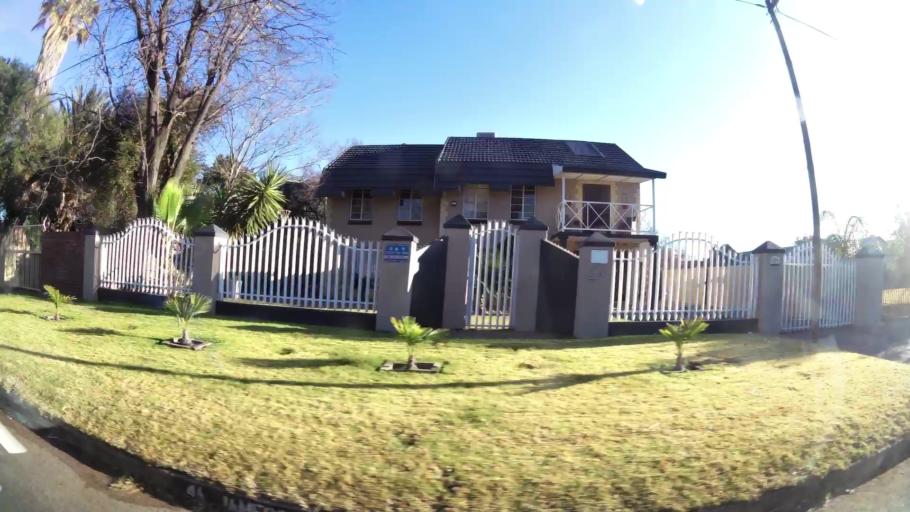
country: ZA
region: Northern Cape
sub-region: Frances Baard District Municipality
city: Kimberley
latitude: -28.7478
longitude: 24.7385
